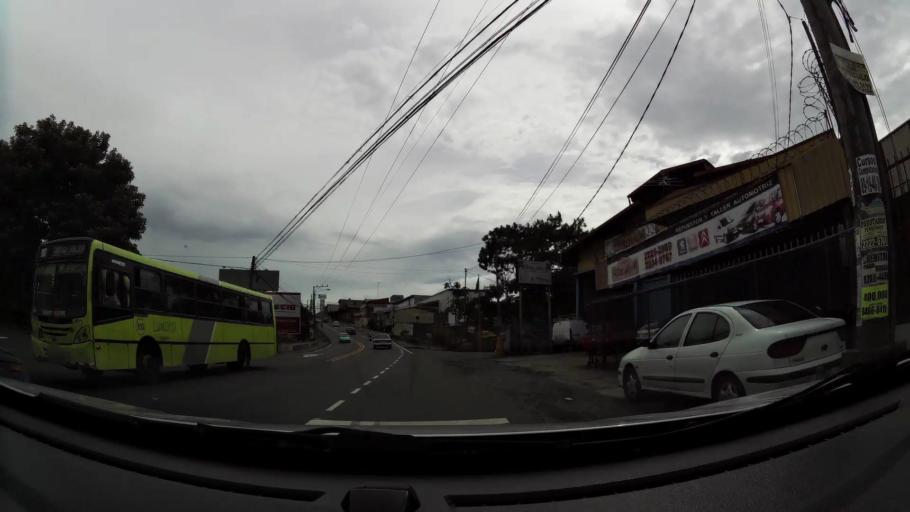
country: CR
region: San Jose
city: Curridabat
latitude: 9.9161
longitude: -84.0403
